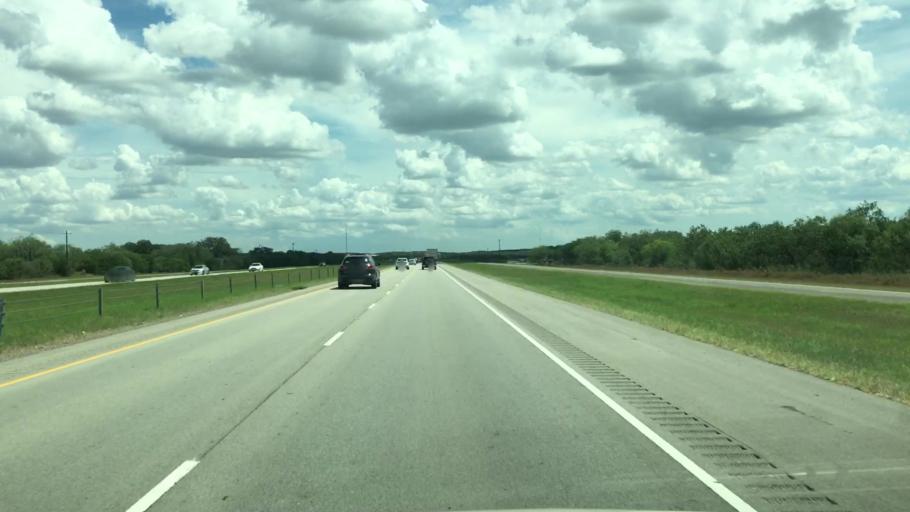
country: US
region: Texas
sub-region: Live Oak County
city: George West
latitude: 28.2741
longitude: -97.9480
